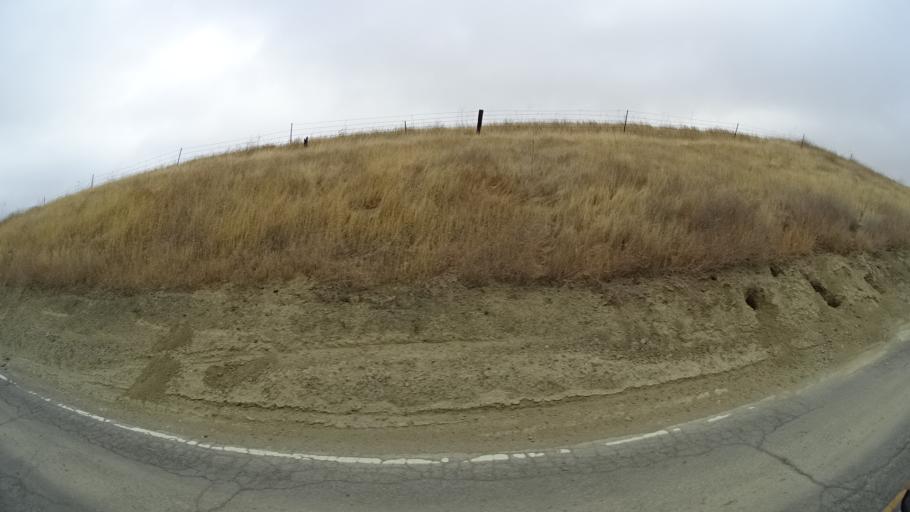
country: US
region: California
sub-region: Yolo County
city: Dunnigan
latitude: 38.8855
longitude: -122.0256
